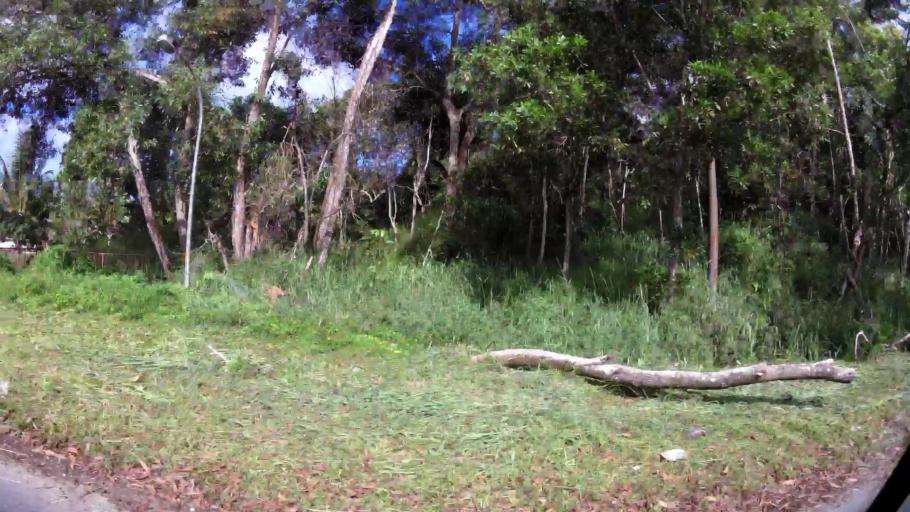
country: BN
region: Brunei and Muara
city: Bandar Seri Begawan
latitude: 4.9226
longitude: 114.8981
